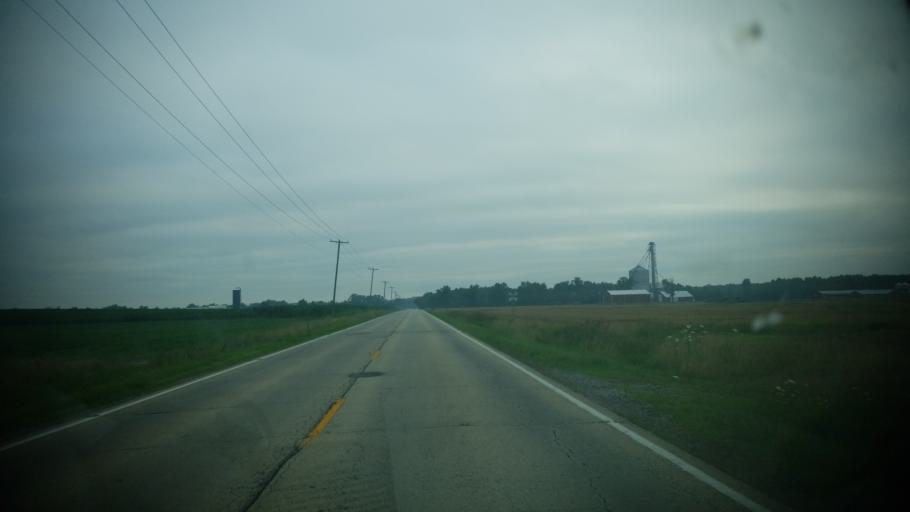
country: US
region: Illinois
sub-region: Clay County
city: Flora
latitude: 38.6608
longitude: -88.4383
